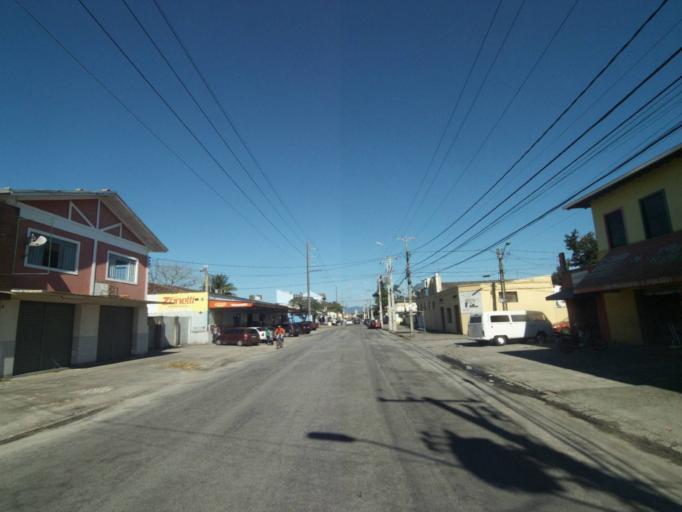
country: BR
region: Parana
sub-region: Paranagua
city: Paranagua
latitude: -25.5213
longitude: -48.5195
